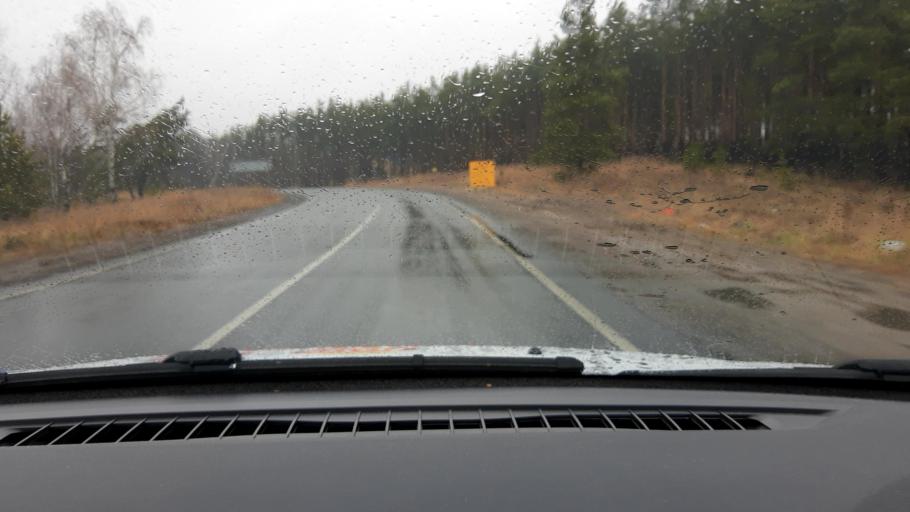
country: RU
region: Nizjnij Novgorod
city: Babino
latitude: 56.2975
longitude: 43.5972
